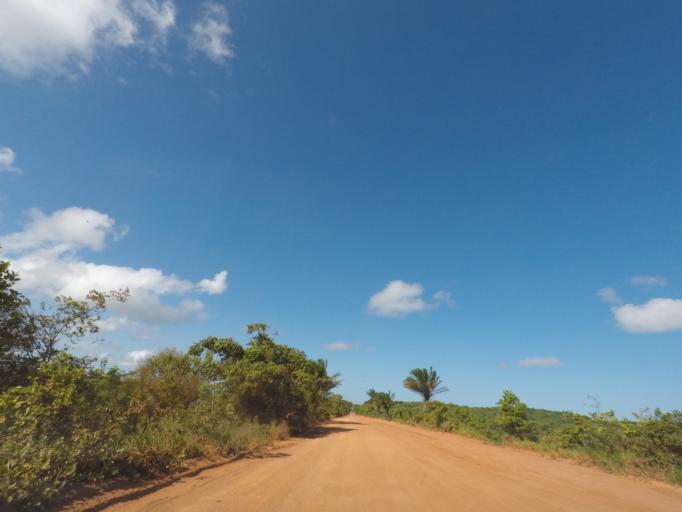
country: BR
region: Bahia
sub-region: Marau
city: Marau
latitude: -14.1429
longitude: -39.0019
